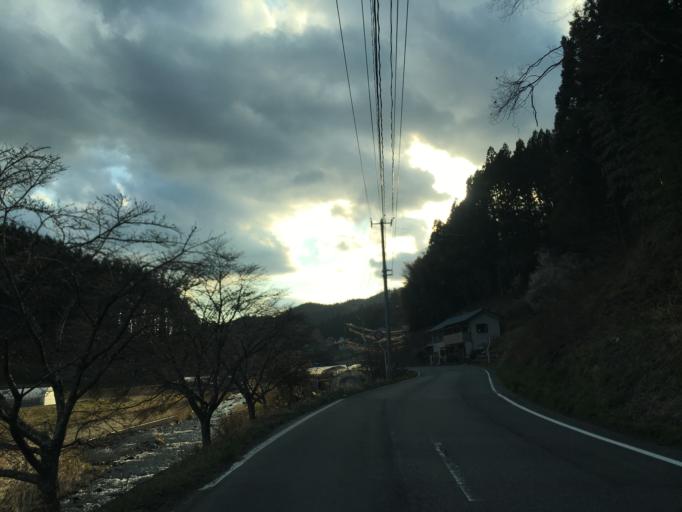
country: JP
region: Fukushima
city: Ishikawa
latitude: 37.0760
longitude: 140.5199
